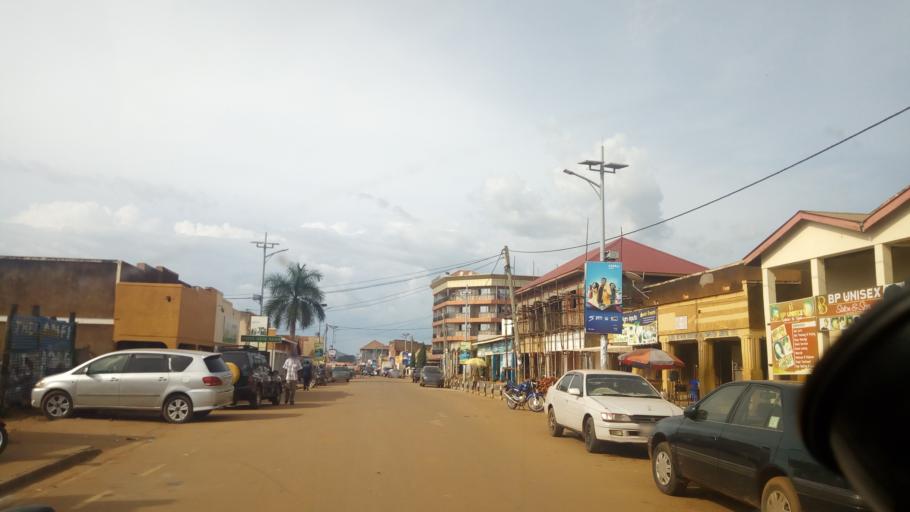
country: UG
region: Northern Region
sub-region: Lira District
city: Lira
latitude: 2.2377
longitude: 32.8921
